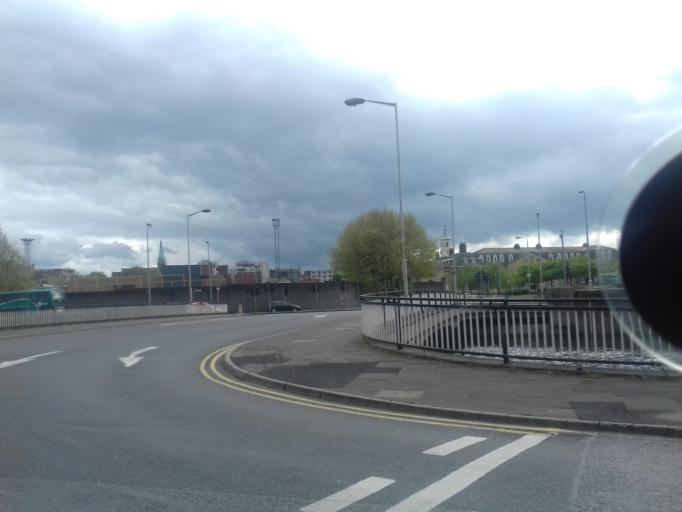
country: IE
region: Leinster
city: Rialto
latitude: 53.3476
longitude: -6.2910
